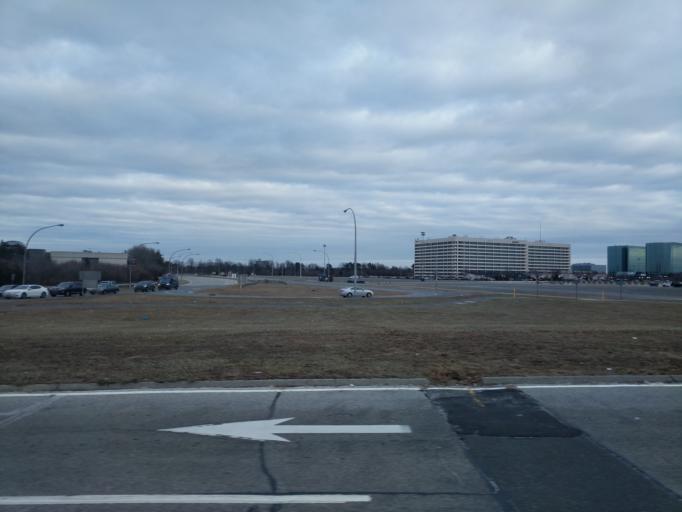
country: US
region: New York
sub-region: Nassau County
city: East Garden City
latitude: 40.7253
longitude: -73.5924
